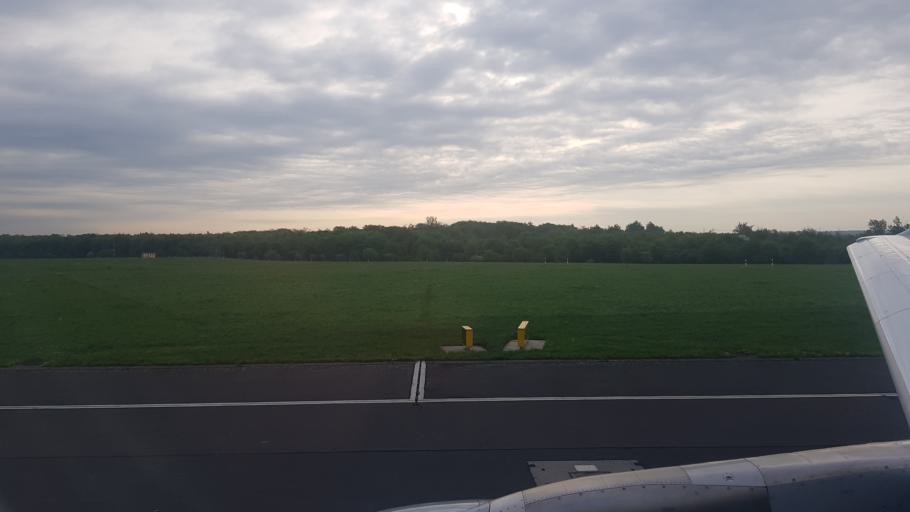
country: DE
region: North Rhine-Westphalia
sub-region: Regierungsbezirk Dusseldorf
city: Ratingen
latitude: 51.2949
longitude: 6.7856
